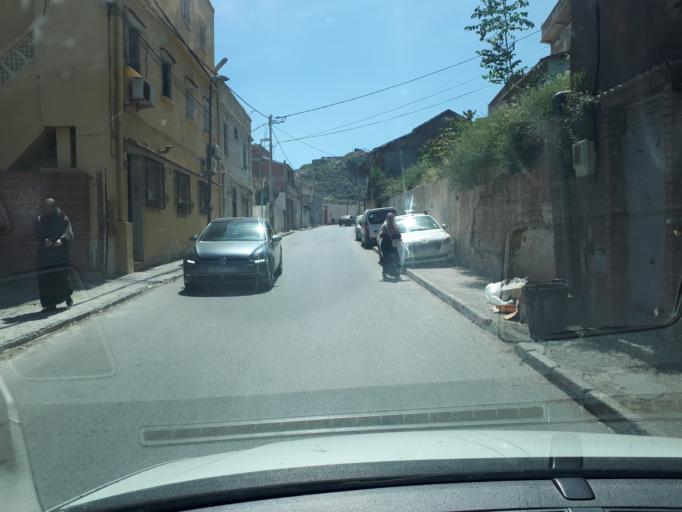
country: DZ
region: Alger
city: Algiers
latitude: 36.8152
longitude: 3.0137
